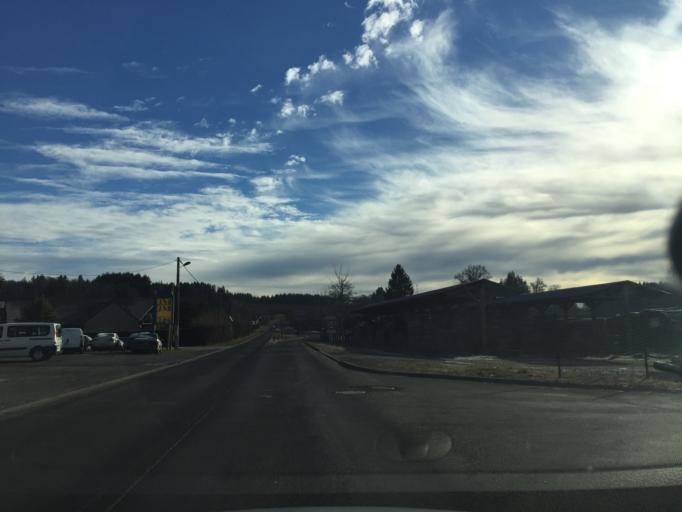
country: FR
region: Limousin
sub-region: Departement de la Creuse
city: Auzances
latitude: 45.8706
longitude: 2.5268
